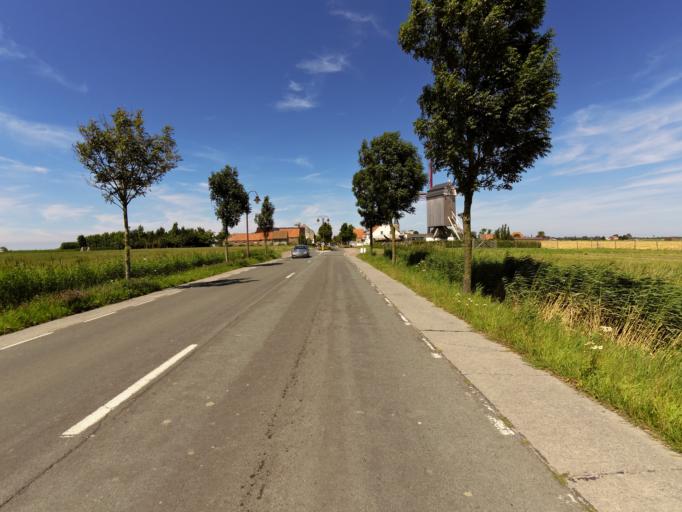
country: BE
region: Flanders
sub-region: Provincie West-Vlaanderen
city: De Haan
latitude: 51.2386
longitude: 3.0277
